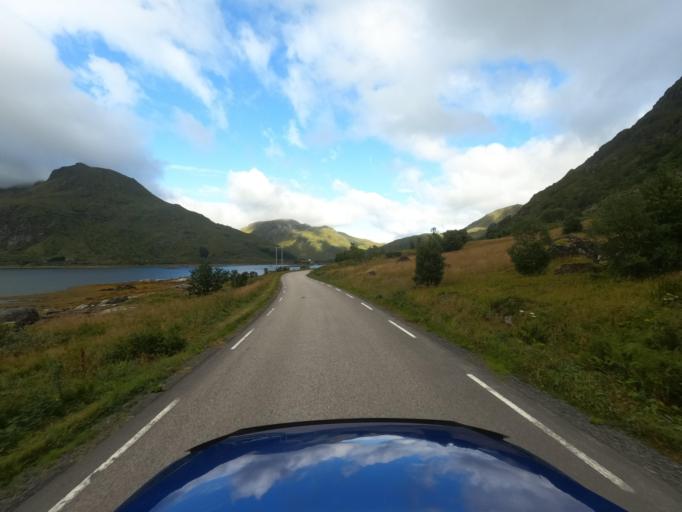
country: NO
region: Nordland
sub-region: Vestvagoy
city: Evjen
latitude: 68.1870
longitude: 13.8927
